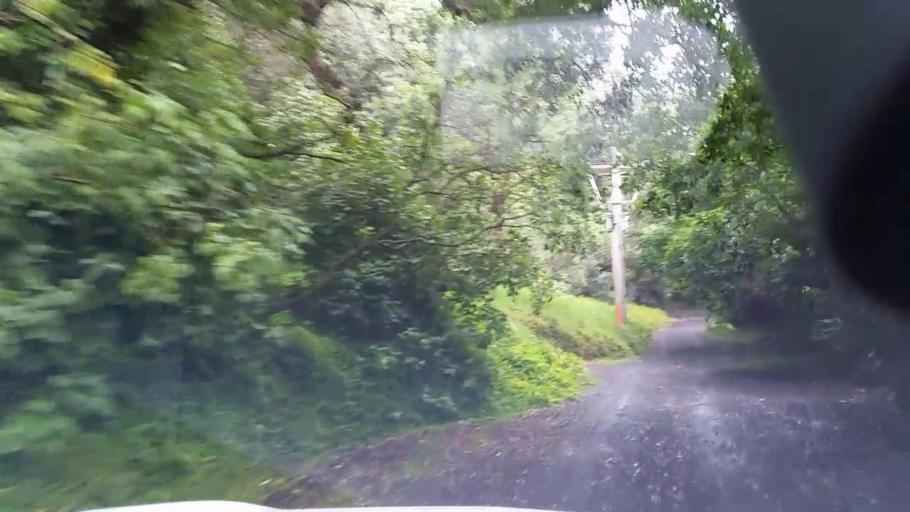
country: NZ
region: Auckland
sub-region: Auckland
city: Muriwai Beach
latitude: -36.9855
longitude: 174.4780
